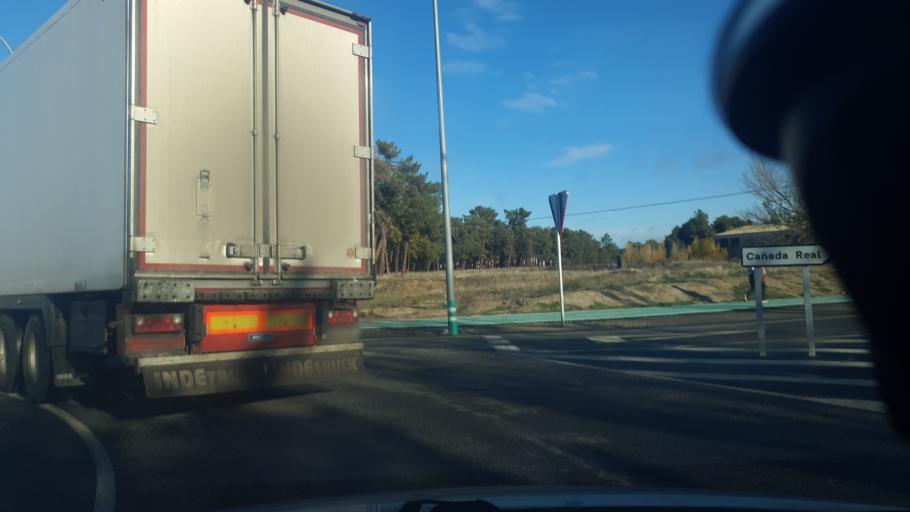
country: ES
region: Castille and Leon
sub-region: Provincia de Avila
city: Arevalo
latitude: 41.0450
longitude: -4.7165
